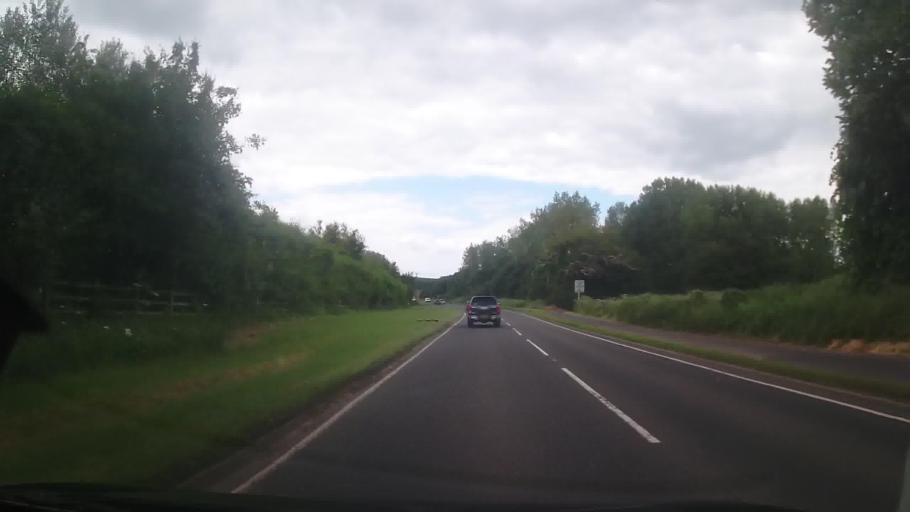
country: GB
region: England
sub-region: Herefordshire
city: Wellington
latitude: 52.1085
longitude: -2.7299
